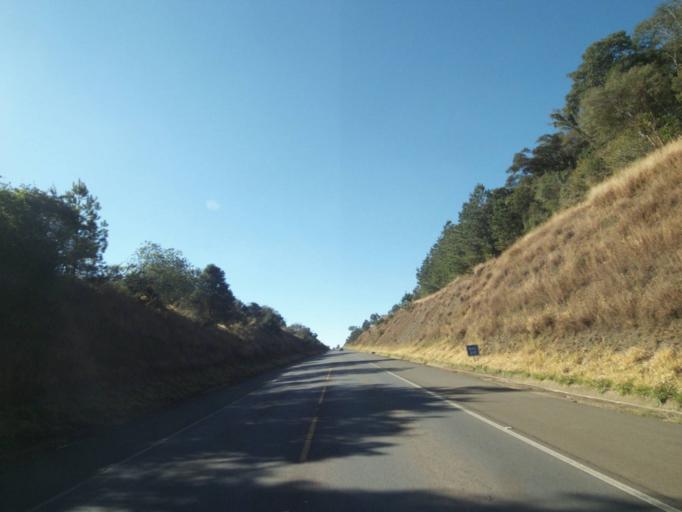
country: BR
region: Parana
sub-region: Tibagi
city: Tibagi
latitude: -24.6071
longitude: -50.4417
